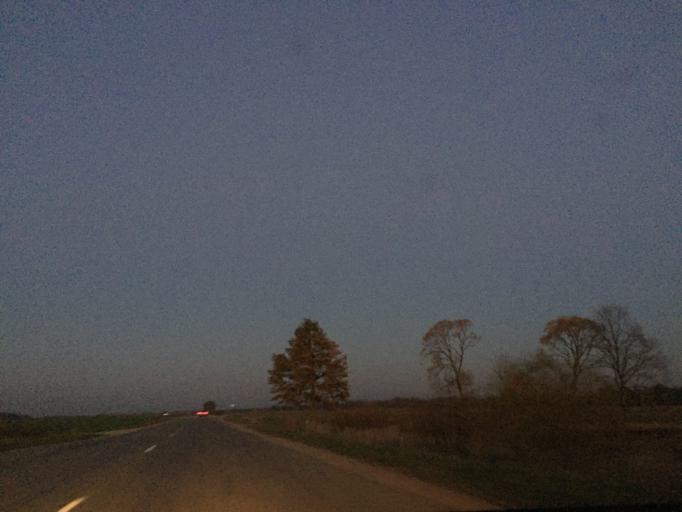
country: LT
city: Zagare
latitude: 56.4910
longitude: 23.2218
